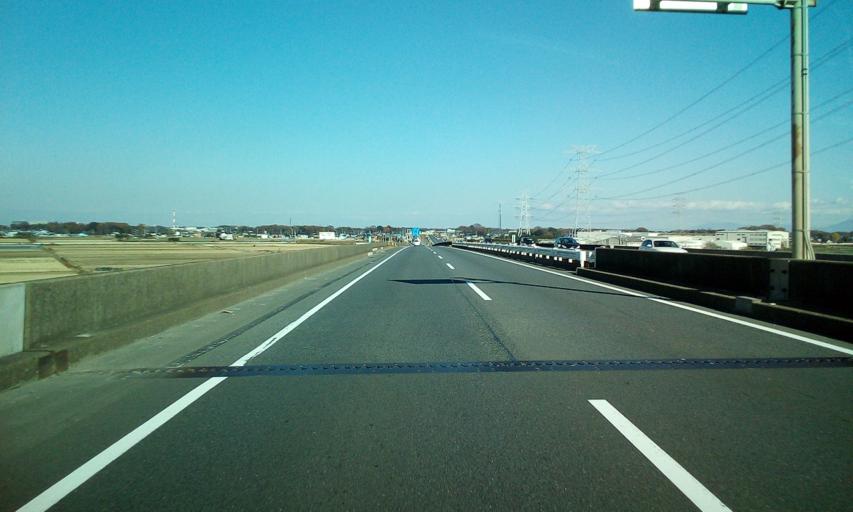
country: JP
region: Ibaraki
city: Sakai
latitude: 36.1288
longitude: 139.7602
